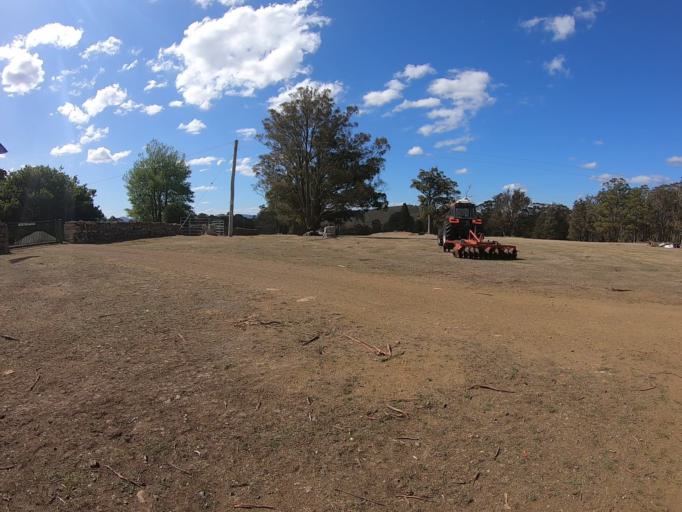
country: AU
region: Tasmania
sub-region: Brighton
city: Bridgewater
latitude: -42.4941
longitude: 147.4139
